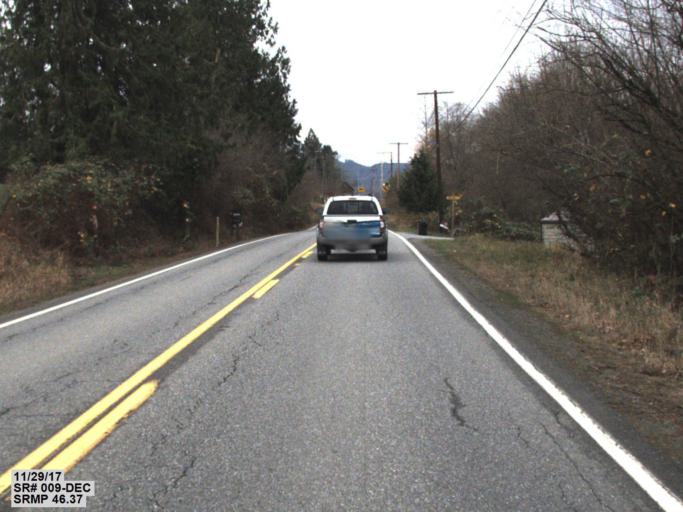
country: US
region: Washington
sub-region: Skagit County
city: Big Lake
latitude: 48.3876
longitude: -122.2316
